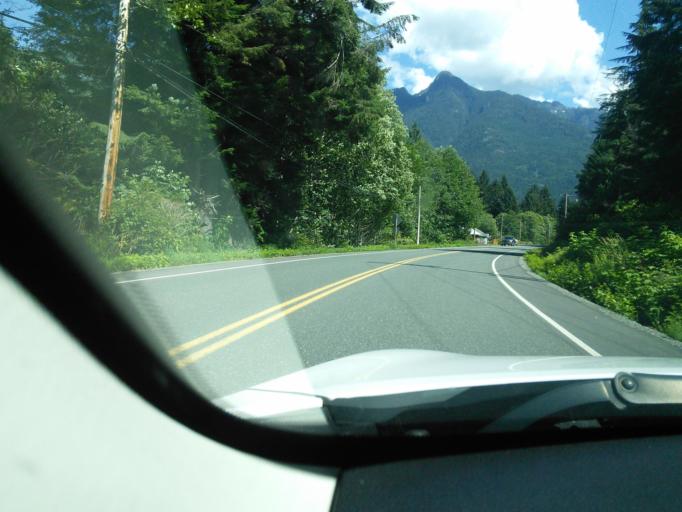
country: CA
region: British Columbia
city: Campbell River
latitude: 50.3631
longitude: -125.9306
